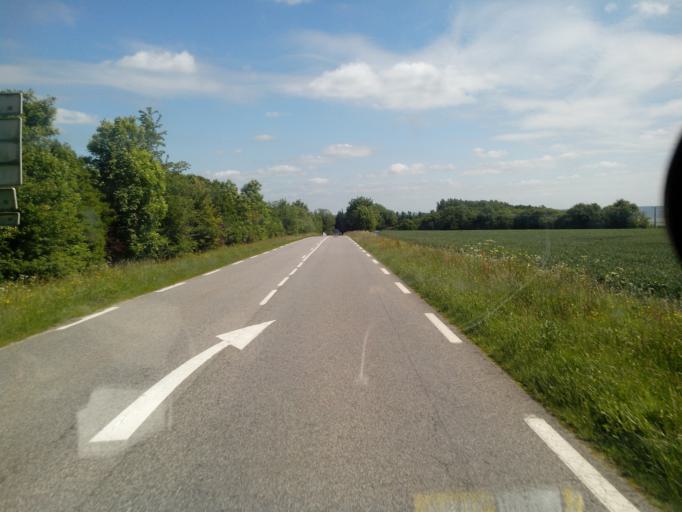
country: FR
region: Haute-Normandie
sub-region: Departement de la Seine-Maritime
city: Tancarville
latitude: 49.4944
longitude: 0.4388
